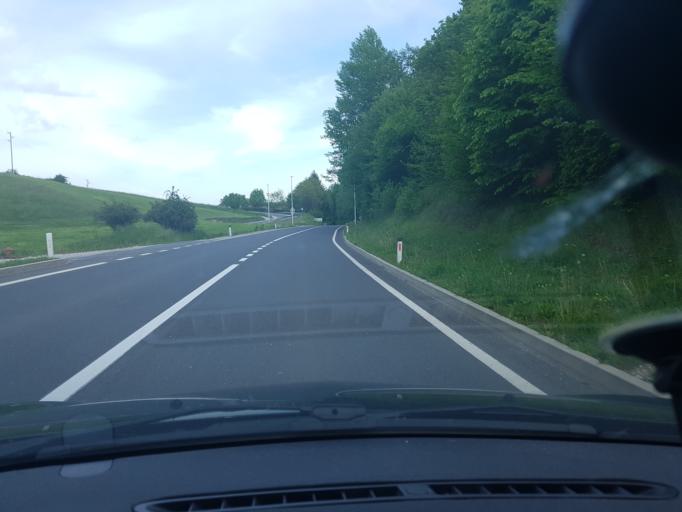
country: SI
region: Rogaska Slatina
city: Rogaska Slatina
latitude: 46.2527
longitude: 15.6259
